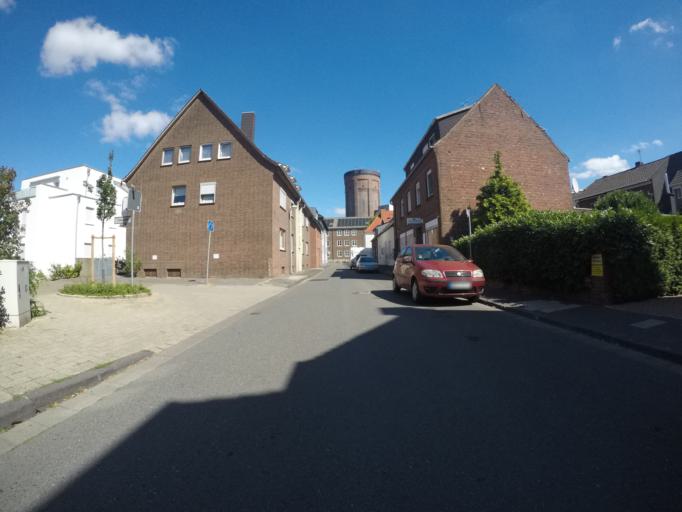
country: DE
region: North Rhine-Westphalia
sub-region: Regierungsbezirk Dusseldorf
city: Bocholt
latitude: 51.8419
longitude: 6.6134
